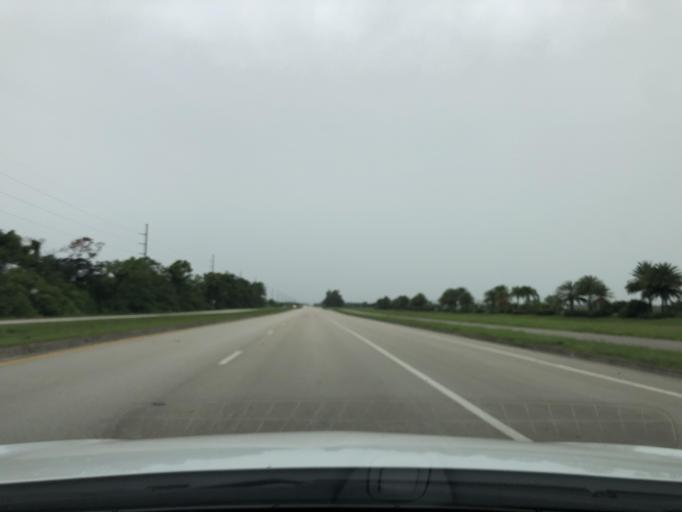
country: US
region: Florida
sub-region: Collier County
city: Immokalee
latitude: 26.2947
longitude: -81.4367
